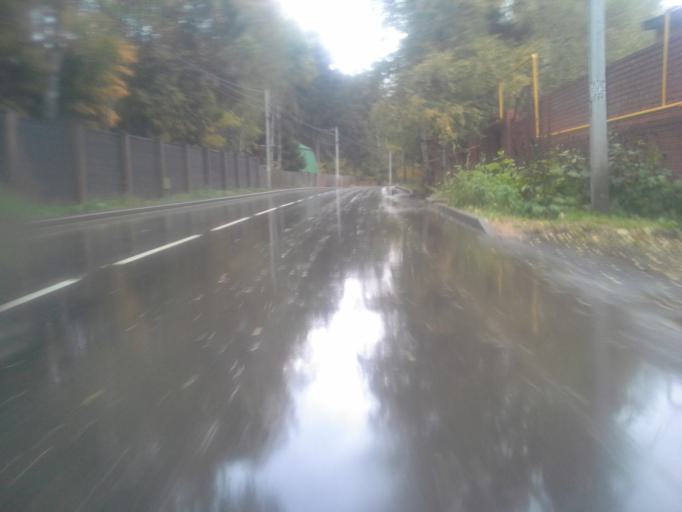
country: RU
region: Moscow
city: Tolstopal'tsevo
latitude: 55.6148
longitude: 37.2052
